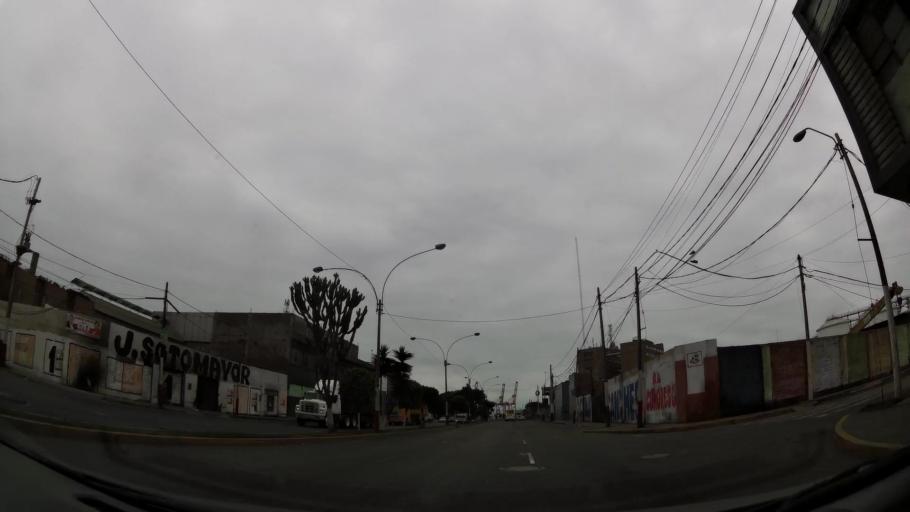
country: PE
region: Callao
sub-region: Callao
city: Callao
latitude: -12.0517
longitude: -77.1373
